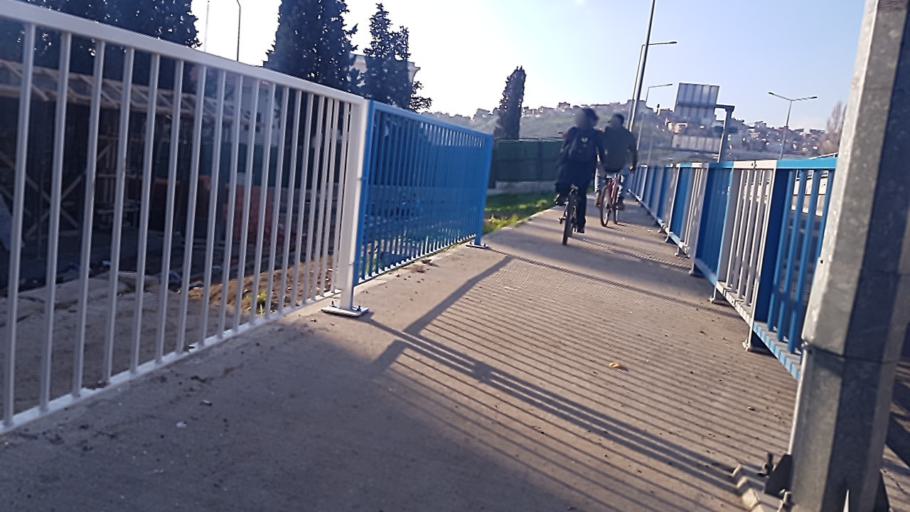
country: TR
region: Izmir
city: Izmir
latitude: 38.4011
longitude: 27.1483
